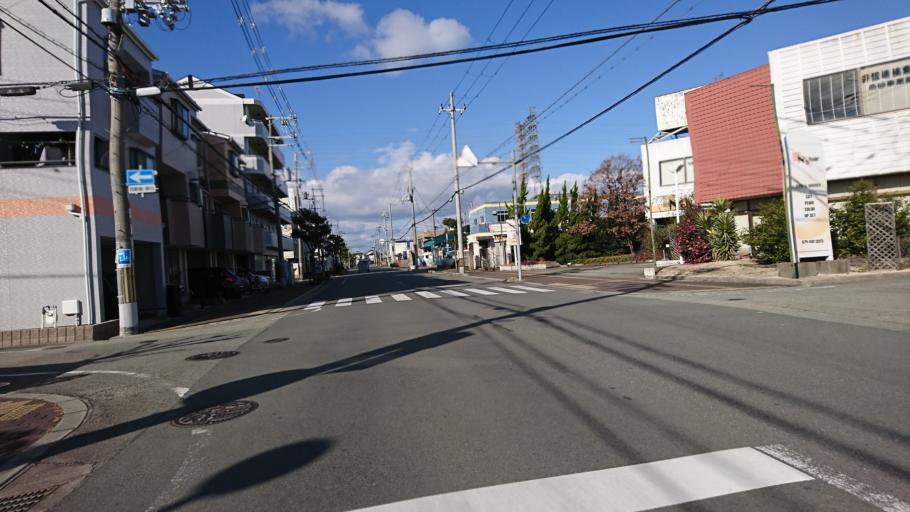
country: JP
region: Hyogo
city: Kakogawacho-honmachi
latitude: 34.7538
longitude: 134.8007
